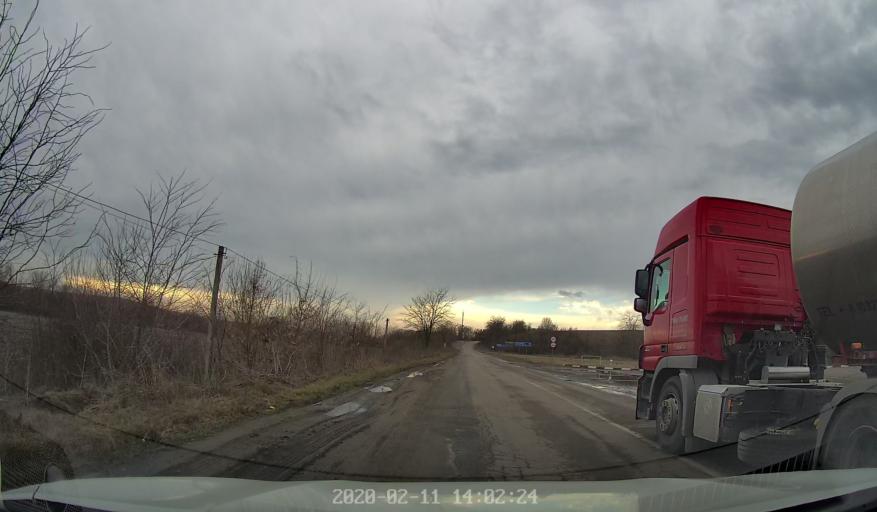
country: RO
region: Botosani
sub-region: Comuna Paltinis
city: Paltinis
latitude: 48.2625
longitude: 26.6140
